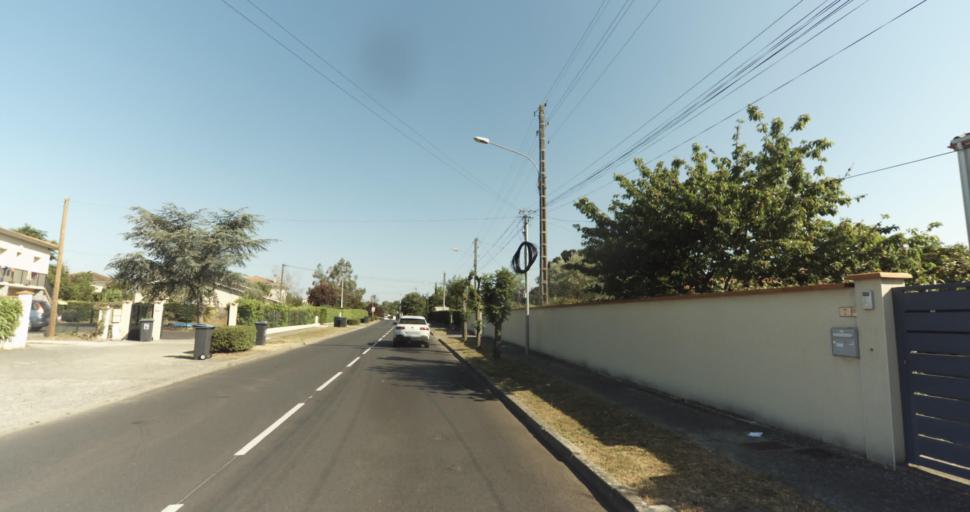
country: FR
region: Midi-Pyrenees
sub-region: Departement de la Haute-Garonne
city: Plaisance-du-Touch
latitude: 43.5589
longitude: 1.3022
